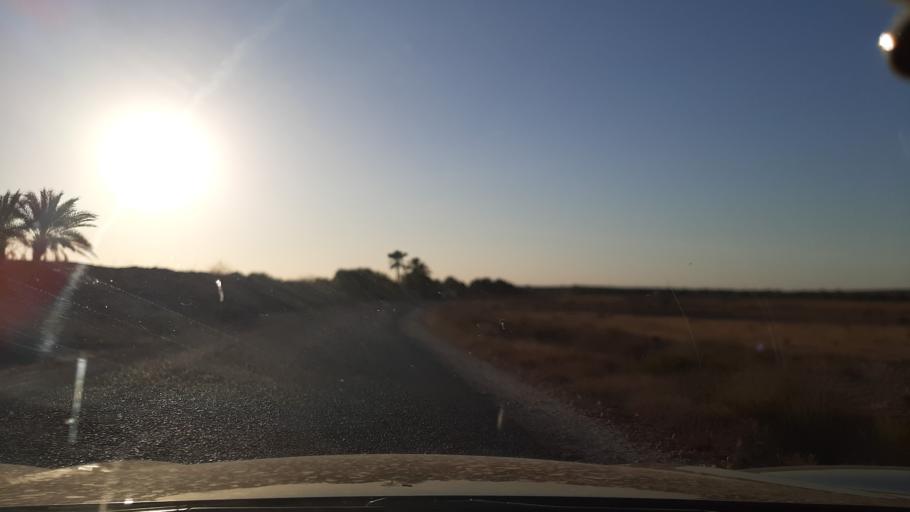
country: TN
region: Qabis
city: Matmata
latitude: 33.6242
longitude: 10.1359
